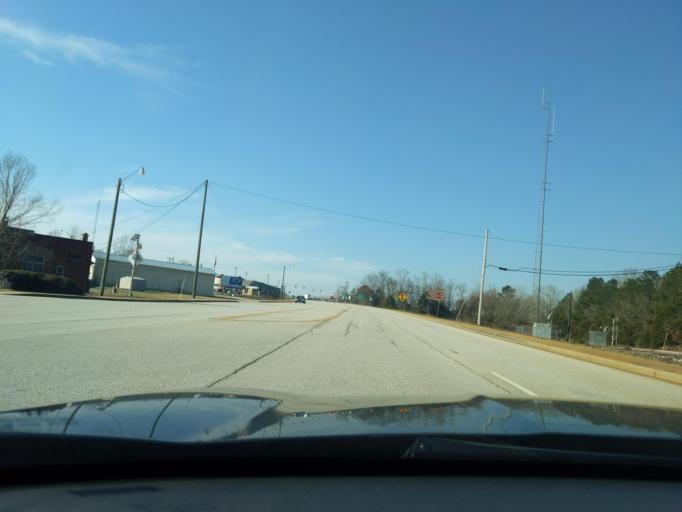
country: US
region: South Carolina
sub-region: Abbeville County
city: Calhoun Falls
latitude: 34.0932
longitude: -82.5953
